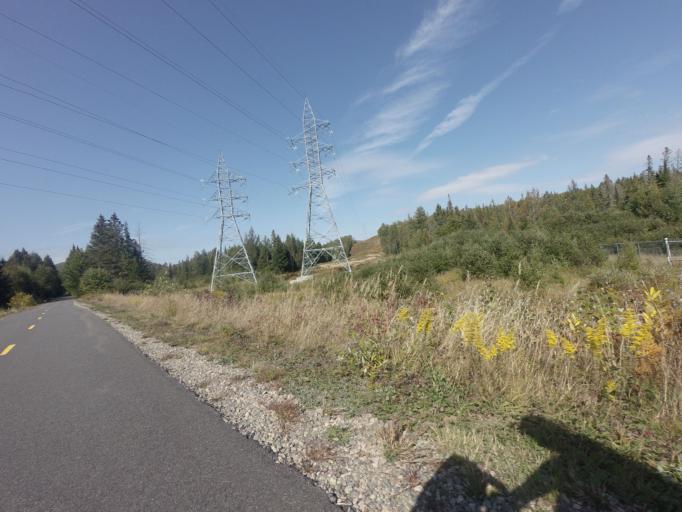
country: CA
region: Quebec
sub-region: Laurentides
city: Mont-Tremblant
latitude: 46.1248
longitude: -74.5444
